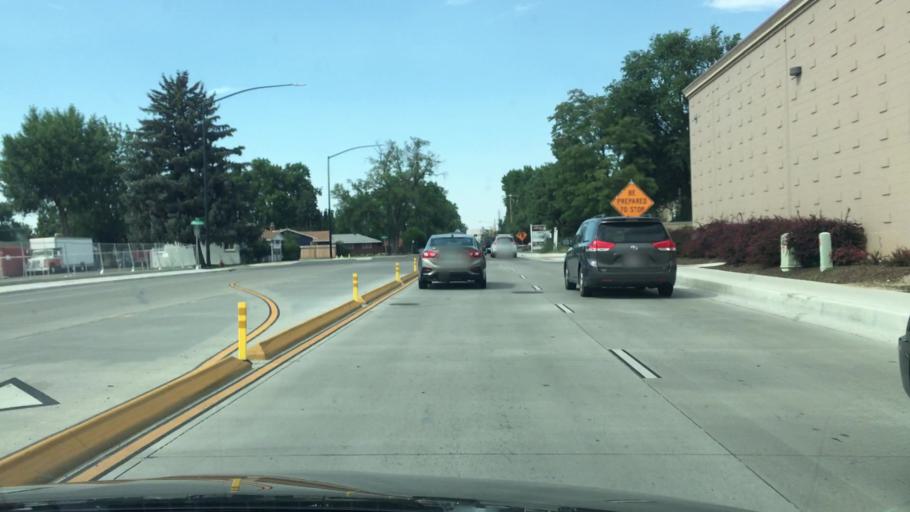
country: US
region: Idaho
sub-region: Ada County
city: Garden City
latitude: 43.6203
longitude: -116.2742
